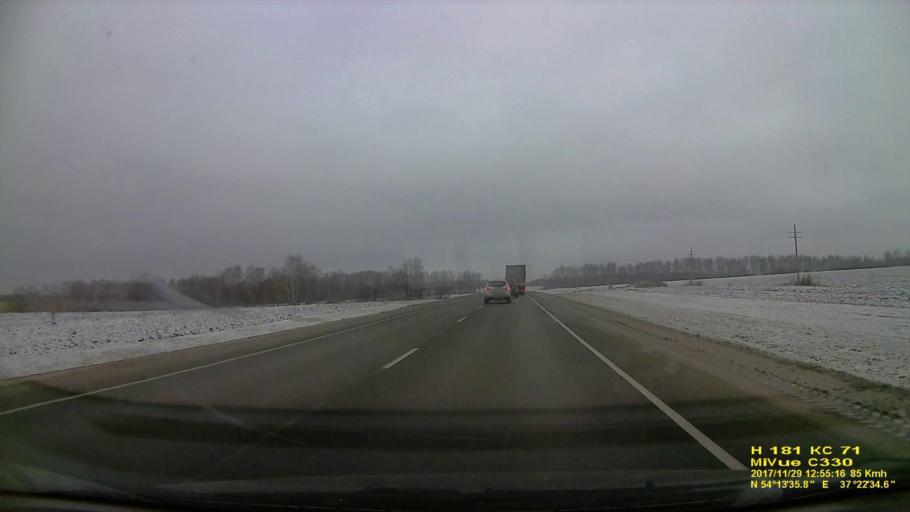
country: RU
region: Tula
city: Leninskiy
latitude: 54.2267
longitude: 37.3761
